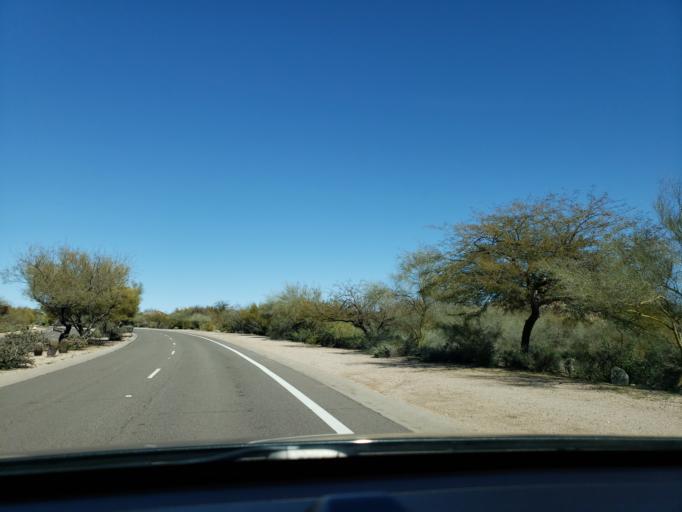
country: US
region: Arizona
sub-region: Maricopa County
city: Carefree
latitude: 33.7071
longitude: -111.8315
